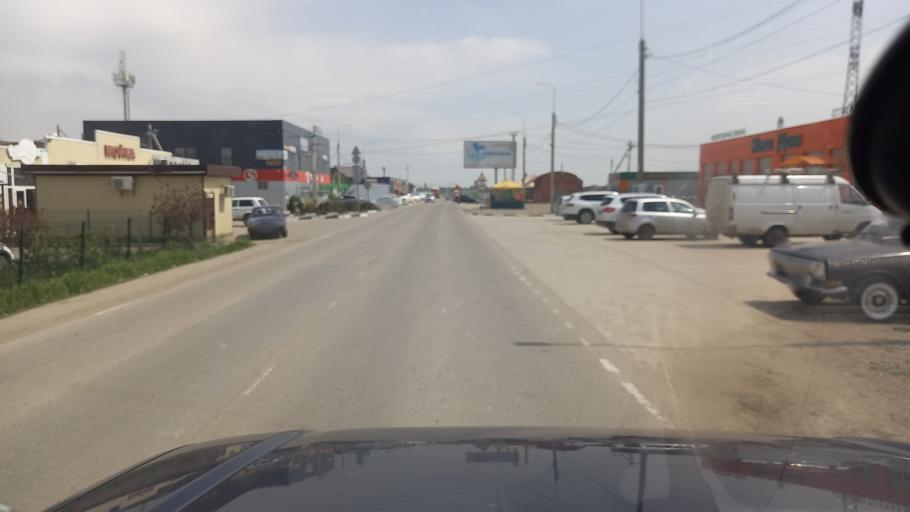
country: RU
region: Adygeya
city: Yablonovskiy
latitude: 44.9858
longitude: 38.9651
